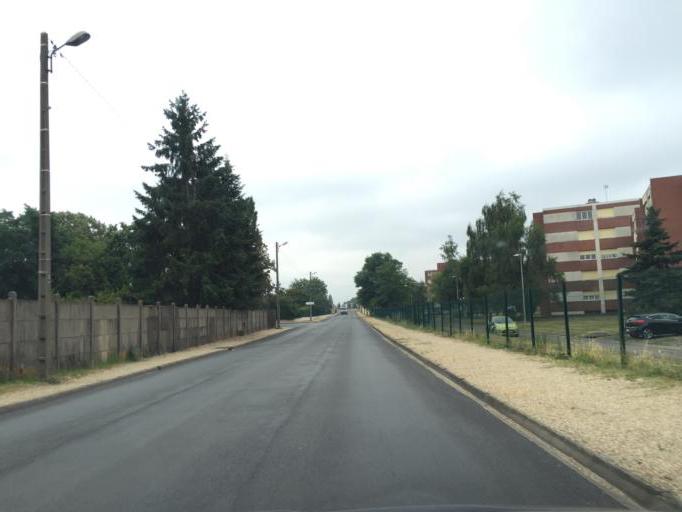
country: FR
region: Auvergne
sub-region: Departement de l'Allier
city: Moulins
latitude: 46.5794
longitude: 3.3275
